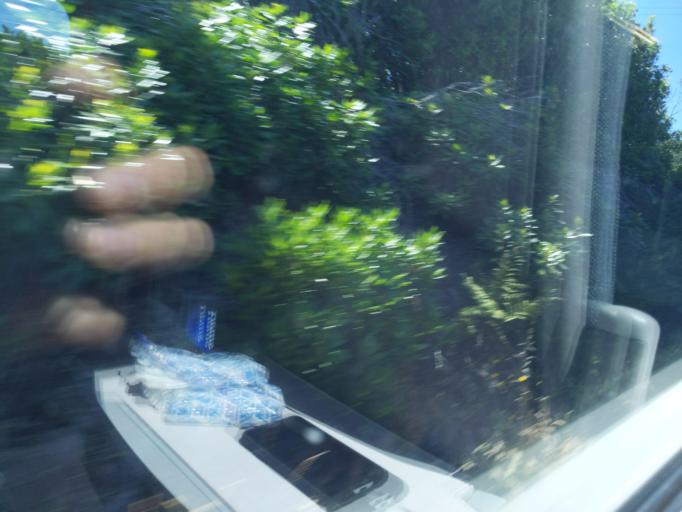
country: GB
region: England
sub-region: Cornwall
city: Chacewater
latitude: 50.2646
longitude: -5.1732
